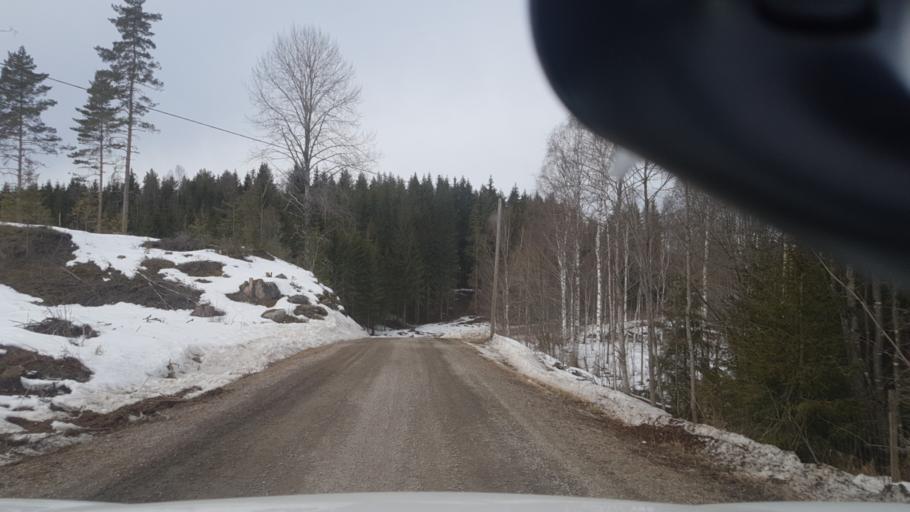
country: SE
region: Vaermland
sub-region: Eda Kommun
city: Amotfors
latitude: 59.8072
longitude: 12.4422
